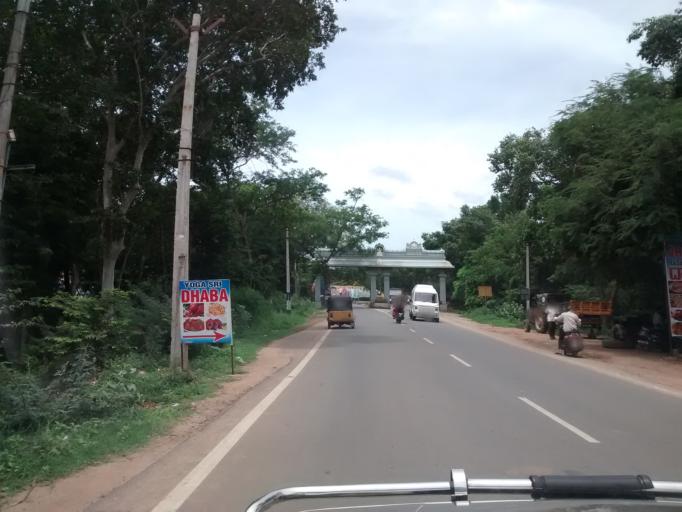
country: IN
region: Andhra Pradesh
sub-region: Chittoor
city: Narasingapuram
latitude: 13.6157
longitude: 79.3633
